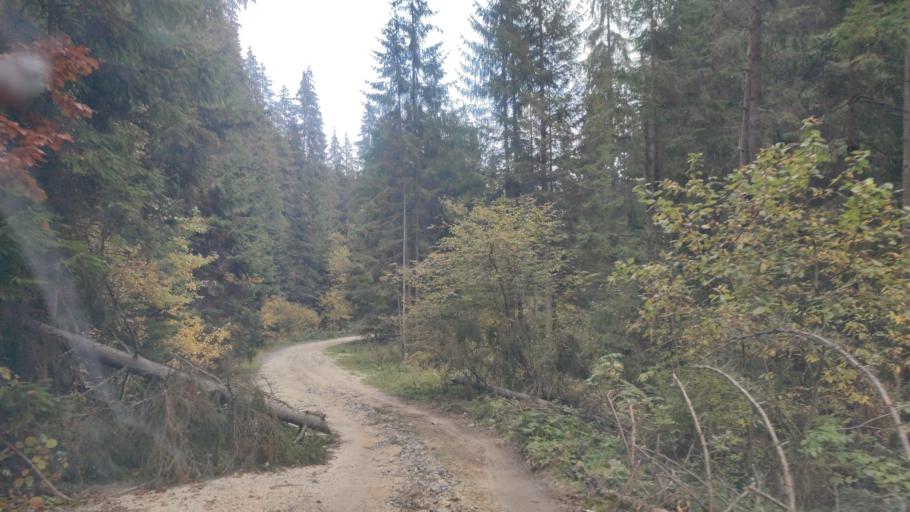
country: RO
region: Harghita
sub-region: Comuna Madaras
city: Madaras
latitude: 46.4720
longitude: 25.6358
